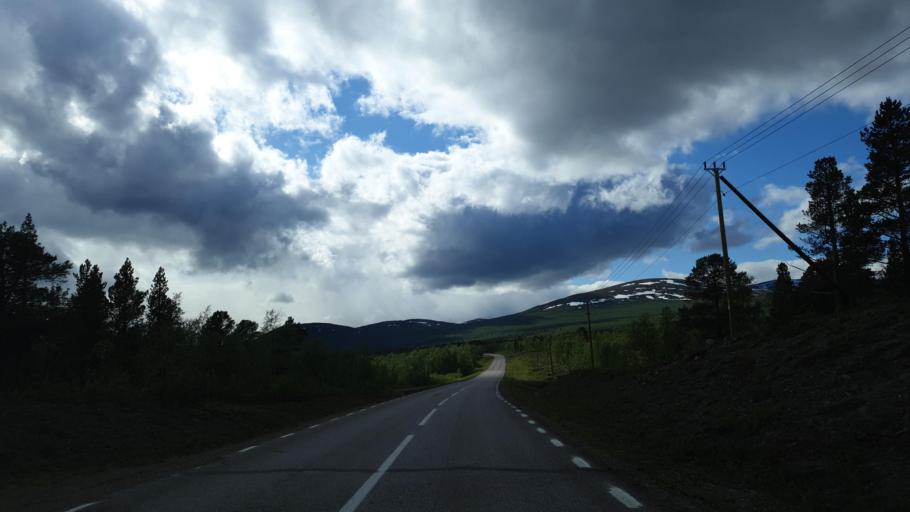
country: SE
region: Norrbotten
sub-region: Kiruna Kommun
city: Kiruna
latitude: 67.8699
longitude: 19.2551
